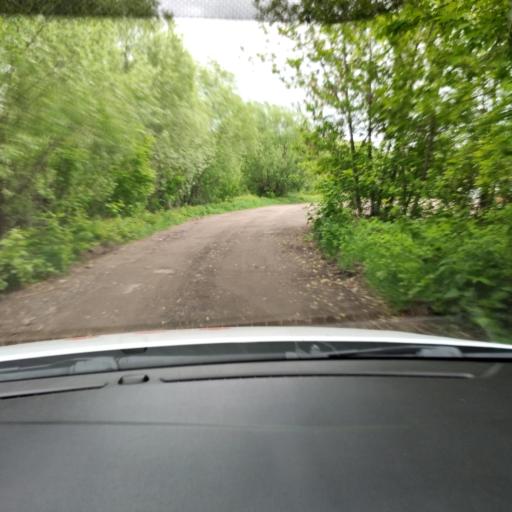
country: RU
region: Tatarstan
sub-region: Gorod Kazan'
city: Kazan
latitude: 55.8101
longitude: 49.2120
